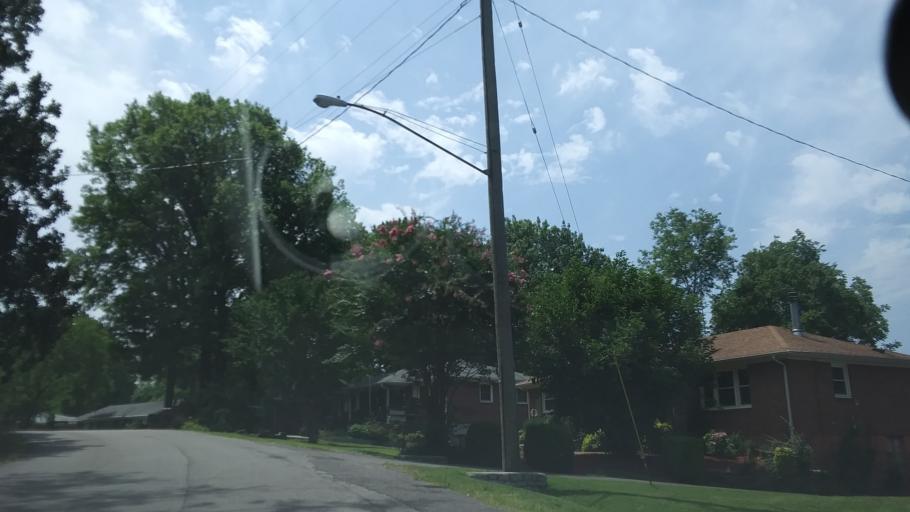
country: US
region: Tennessee
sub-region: Davidson County
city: Belle Meade
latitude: 36.1524
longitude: -86.8791
